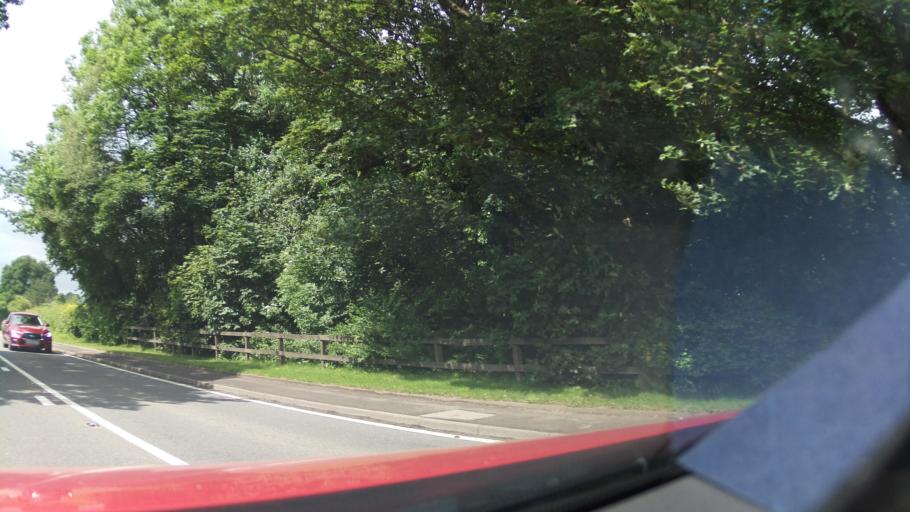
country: GB
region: England
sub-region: Derbyshire
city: Shirley
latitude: 52.9929
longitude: -1.6916
